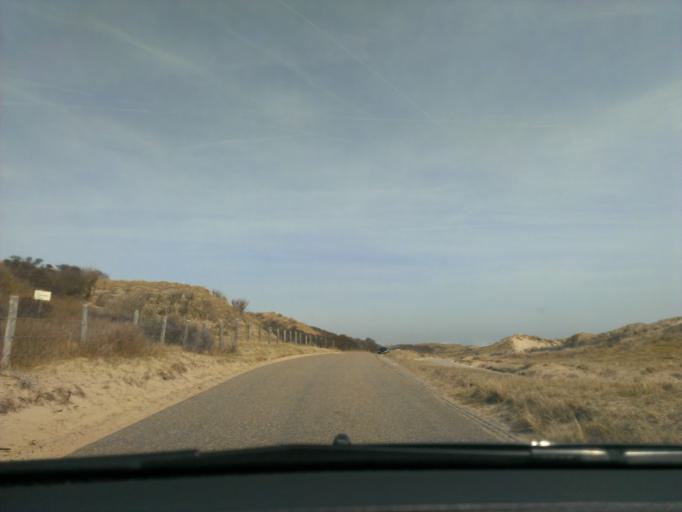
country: NL
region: North Holland
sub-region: Gemeente Zandvoort
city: Zandvoort
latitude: 52.4108
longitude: 4.5503
